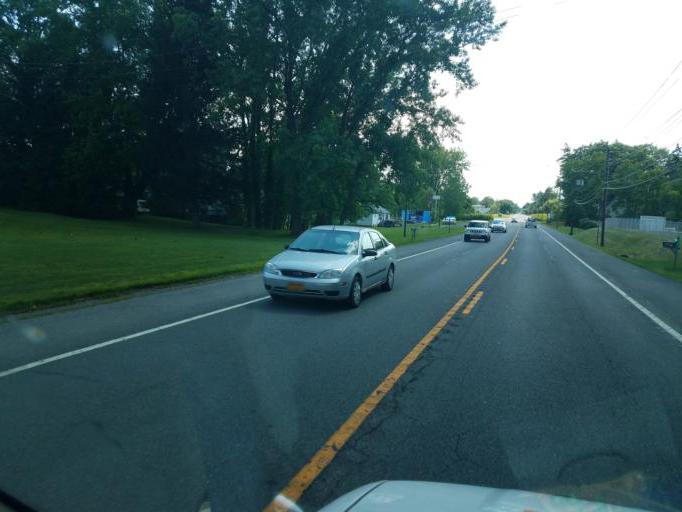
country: US
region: New York
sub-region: Seneca County
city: Waterloo
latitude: 42.8916
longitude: -76.9214
